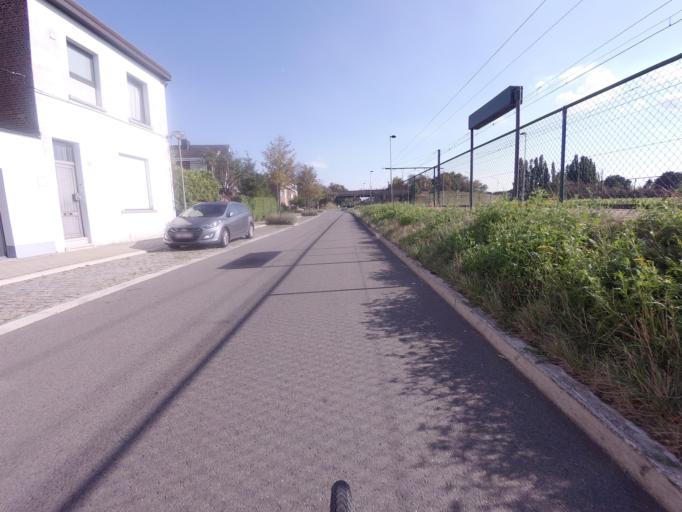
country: BE
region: Flanders
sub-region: Provincie Antwerpen
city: Kapellen
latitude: 51.2911
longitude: 4.4366
